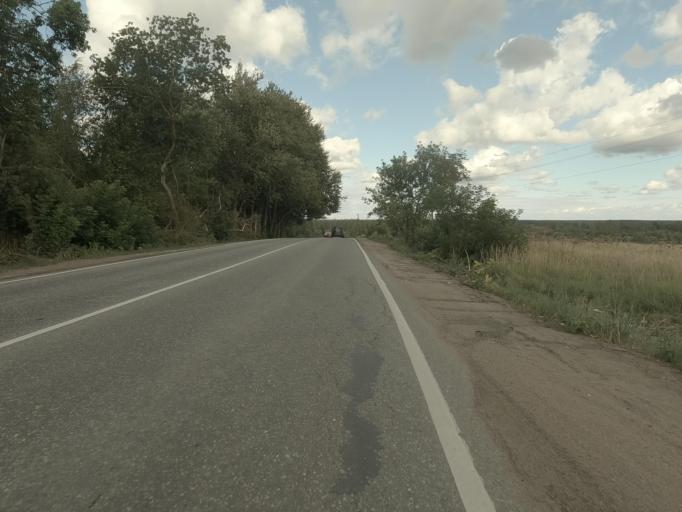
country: RU
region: Leningrad
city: Shcheglovo
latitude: 60.0273
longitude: 30.7623
